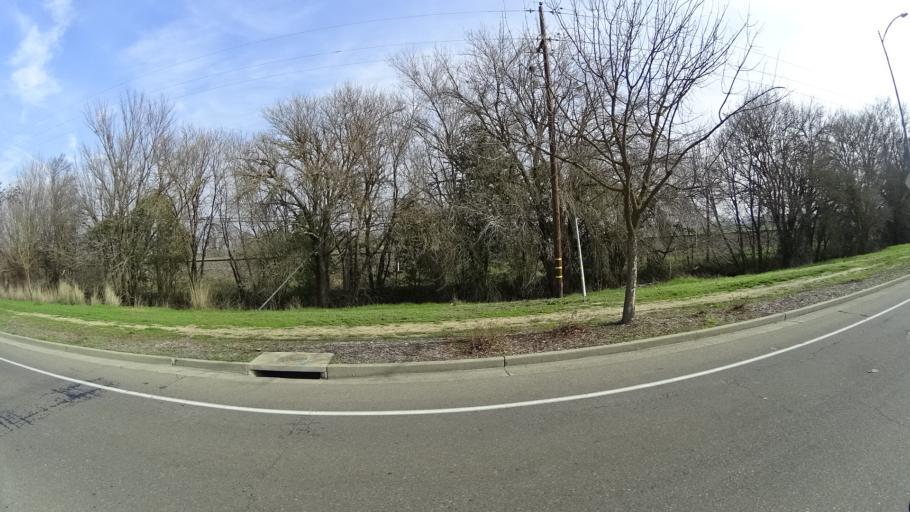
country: US
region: California
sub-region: Yolo County
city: Davis
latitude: 38.5706
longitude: -121.7467
